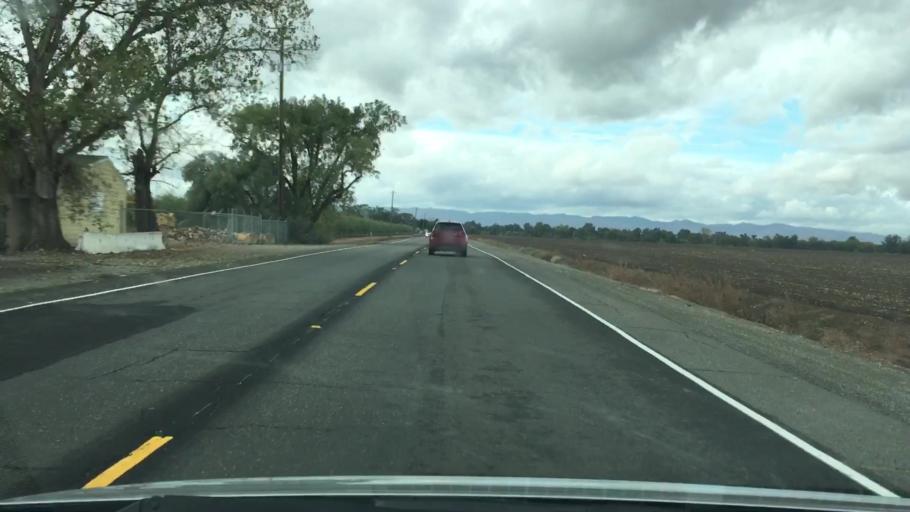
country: US
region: California
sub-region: Yolo County
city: Davis
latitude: 38.5616
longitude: -121.8320
